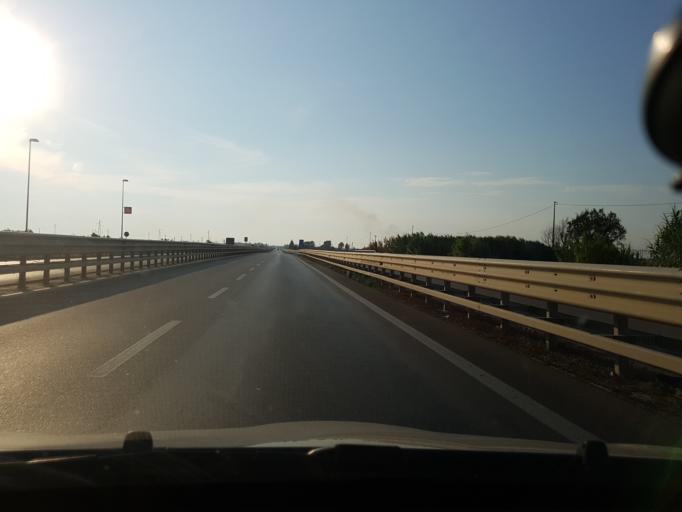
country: IT
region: Apulia
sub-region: Provincia di Foggia
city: Orta Nova
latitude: 41.3487
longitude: 15.7306
